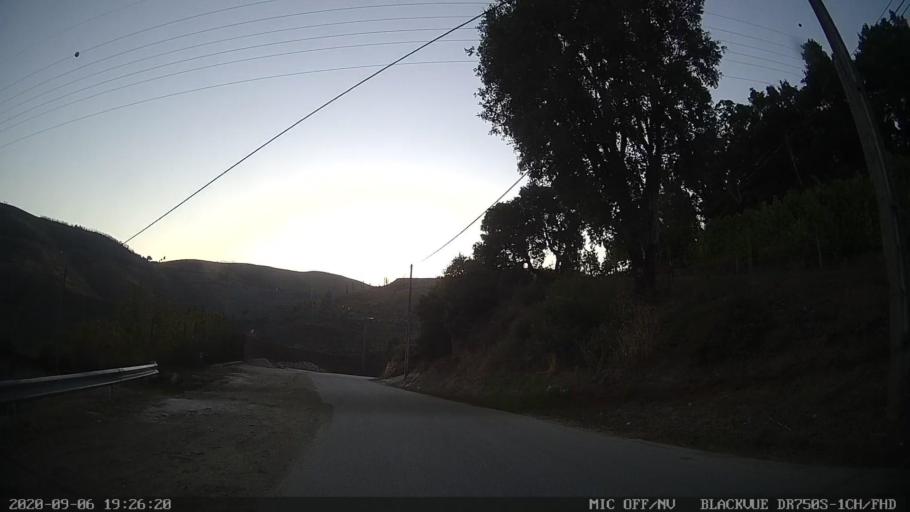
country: PT
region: Vila Real
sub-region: Mesao Frio
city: Mesao Frio
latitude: 41.1827
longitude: -7.9192
